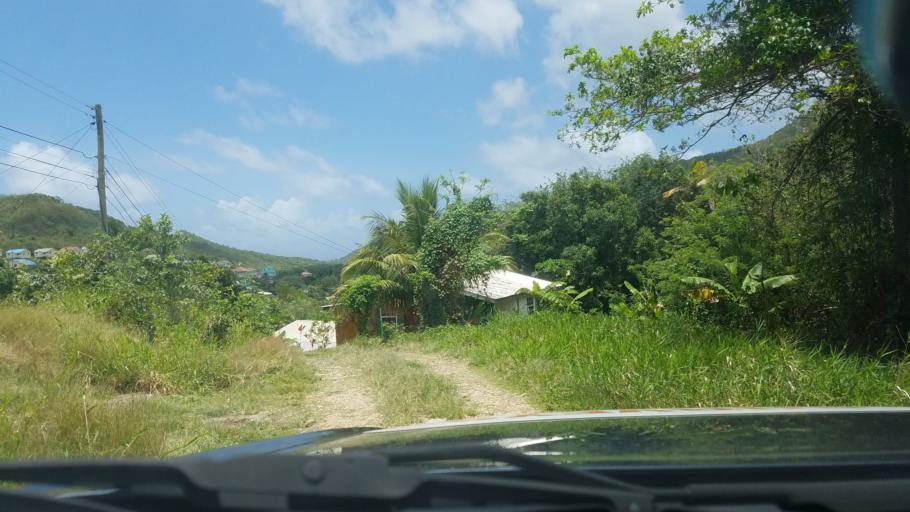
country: LC
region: Gros-Islet
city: Gros Islet
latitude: 14.0548
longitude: -60.9333
